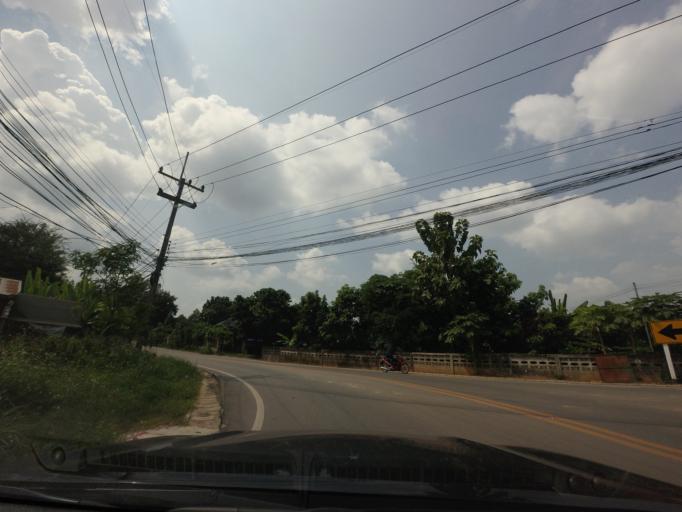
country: TH
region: Nan
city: Pua
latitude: 19.1565
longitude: 100.9317
